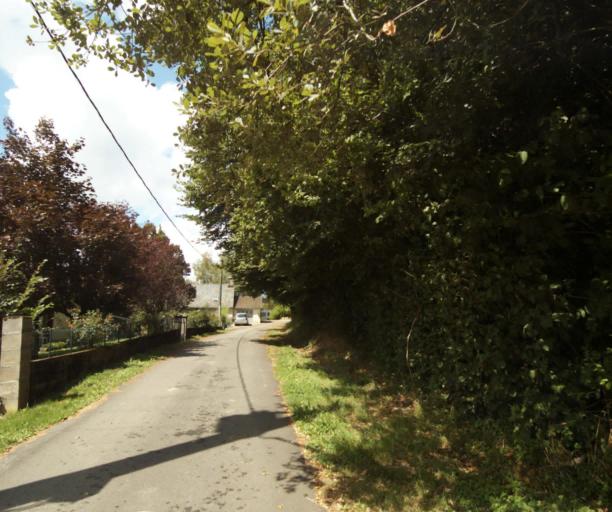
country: FR
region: Limousin
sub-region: Departement de la Correze
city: Sainte-Fortunade
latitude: 45.1737
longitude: 1.8259
